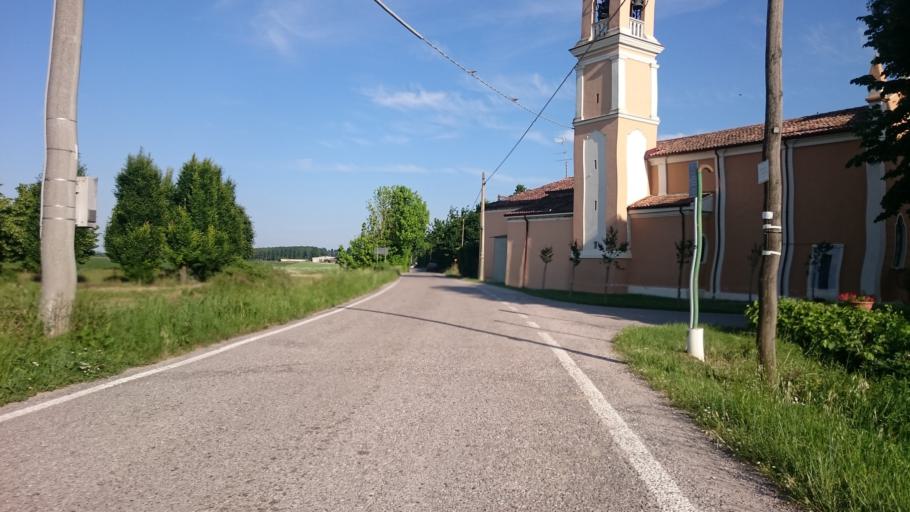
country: IT
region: Lombardy
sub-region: Provincia di Mantova
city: Roncoferraro
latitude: 45.1510
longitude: 10.9768
